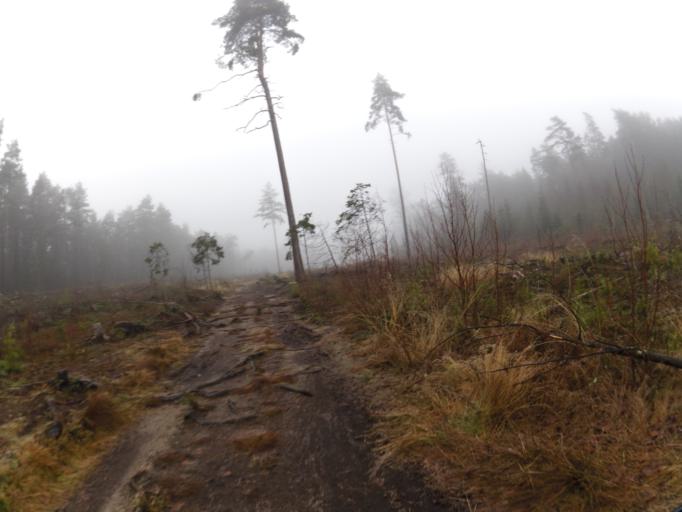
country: NO
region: Ostfold
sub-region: Fredrikstad
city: Fredrikstad
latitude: 59.2610
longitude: 10.9810
